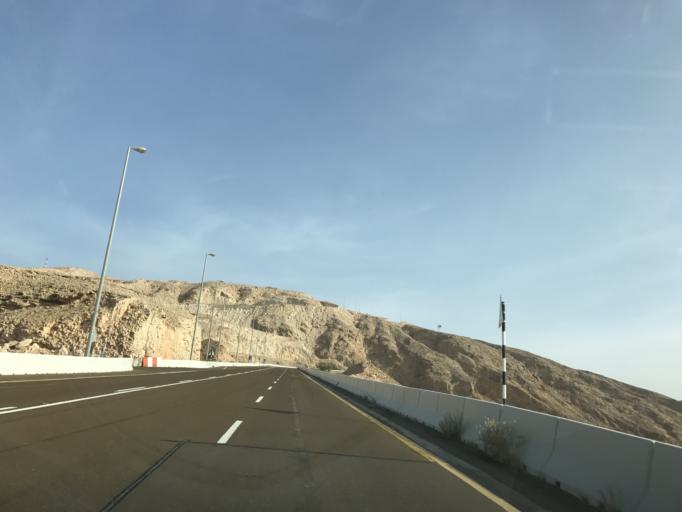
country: AE
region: Abu Dhabi
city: Al Ain
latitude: 24.0901
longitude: 55.7630
